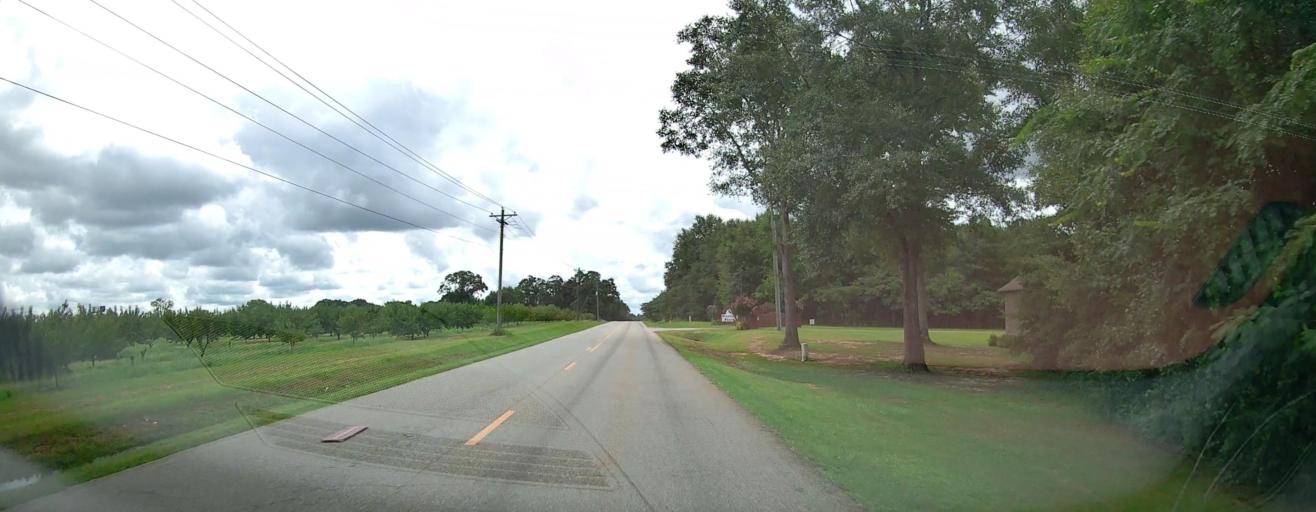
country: US
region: Georgia
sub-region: Peach County
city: Byron
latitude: 32.5973
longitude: -83.7482
